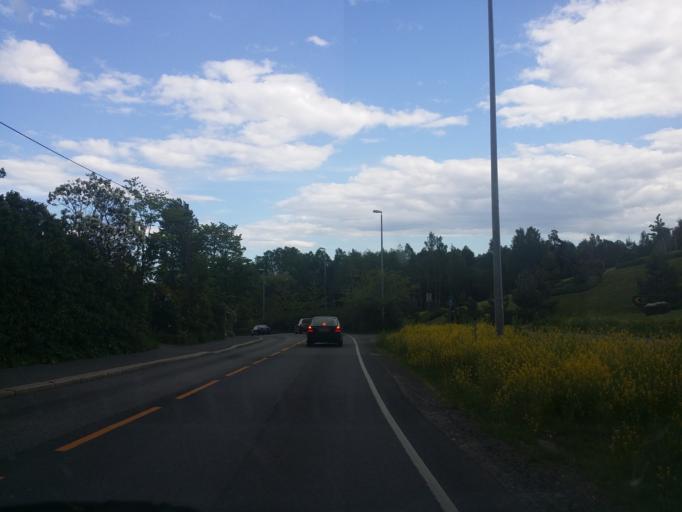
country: NO
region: Oslo
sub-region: Oslo
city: Sjolyststranda
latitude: 59.9432
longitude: 10.6623
